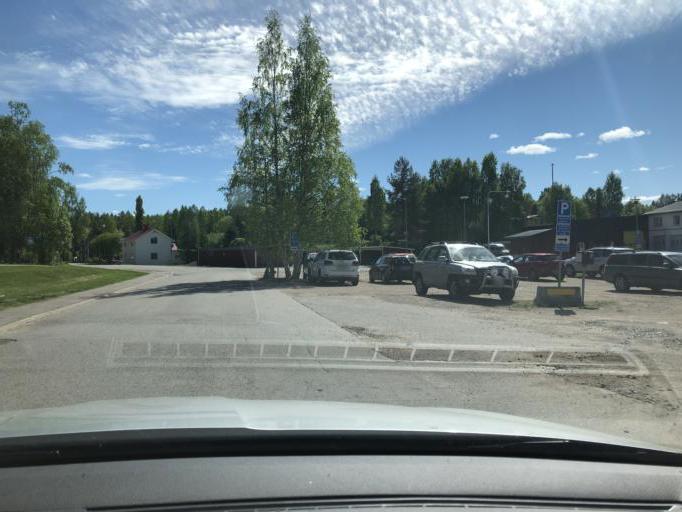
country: SE
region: Norrbotten
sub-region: Alvsbyns Kommun
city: AElvsbyn
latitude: 65.6705
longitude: 21.0092
